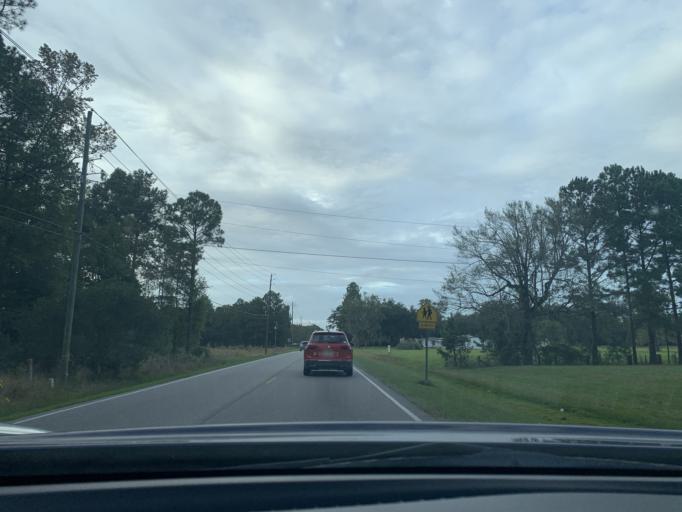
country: US
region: Georgia
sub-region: Chatham County
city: Pooler
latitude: 32.0630
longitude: -81.2719
